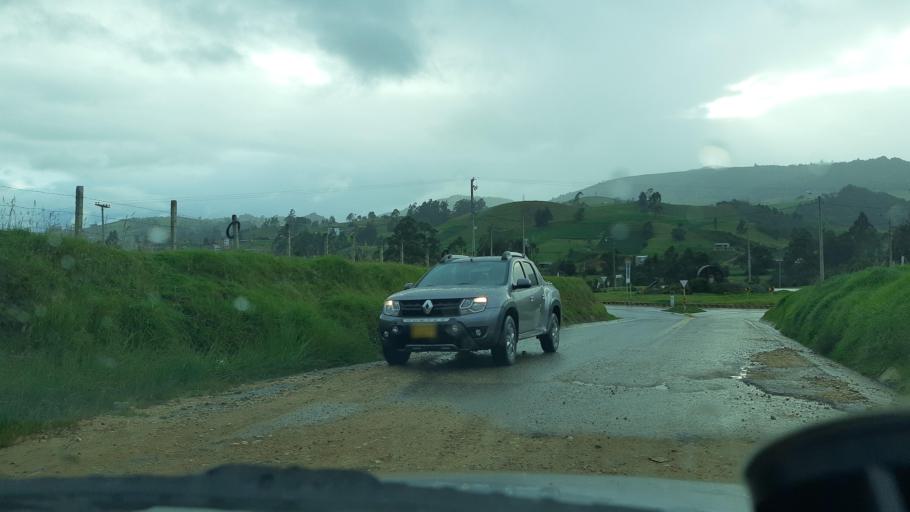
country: CO
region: Cundinamarca
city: Villapinzon
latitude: 5.2246
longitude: -73.5895
